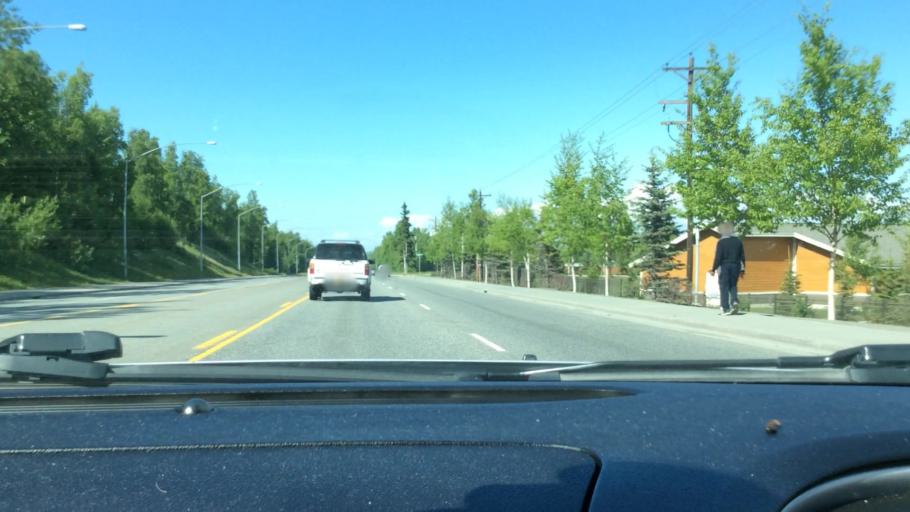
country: US
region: Alaska
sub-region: Anchorage Municipality
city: Anchorage
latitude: 61.2119
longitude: -149.7784
